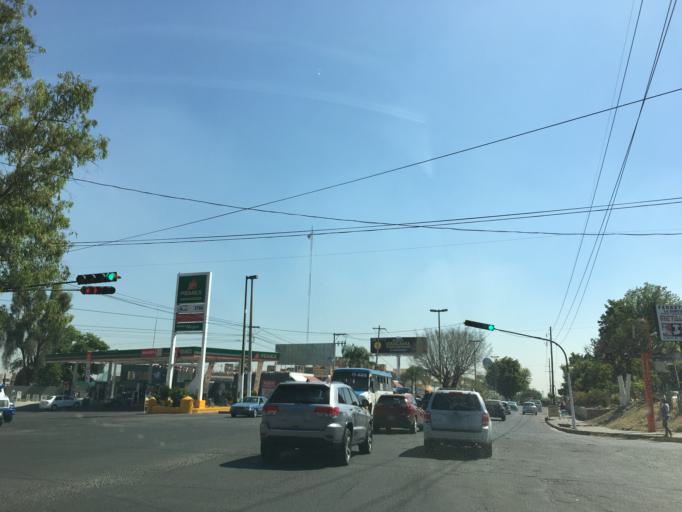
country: MX
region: Jalisco
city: Guadalajara
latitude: 20.6276
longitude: -103.4103
